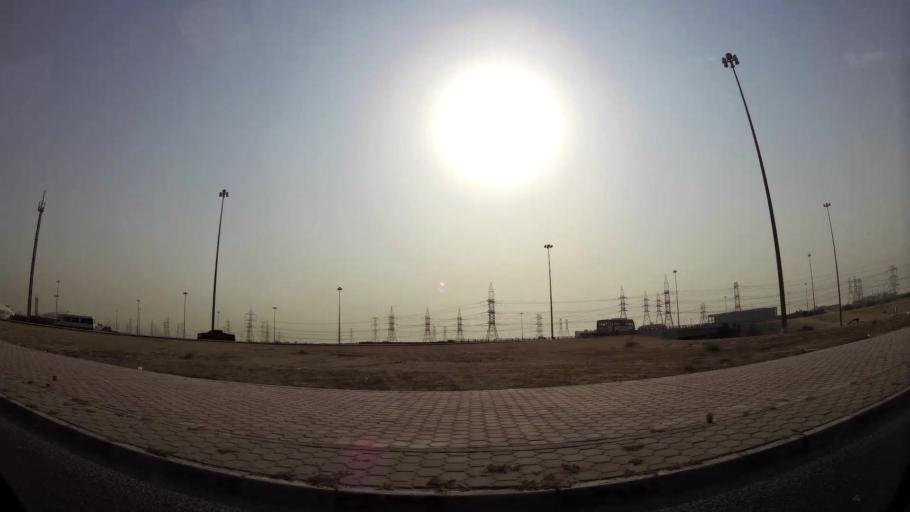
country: KW
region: Al Ahmadi
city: Al Ahmadi
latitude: 29.0937
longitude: 48.0993
